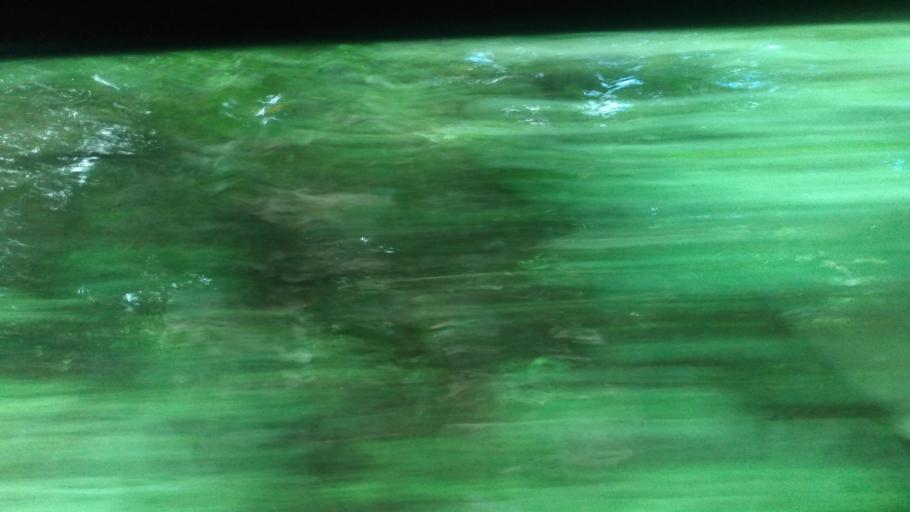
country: BR
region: Pernambuco
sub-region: Quipapa
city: Quipapa
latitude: -8.7809
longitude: -35.9489
